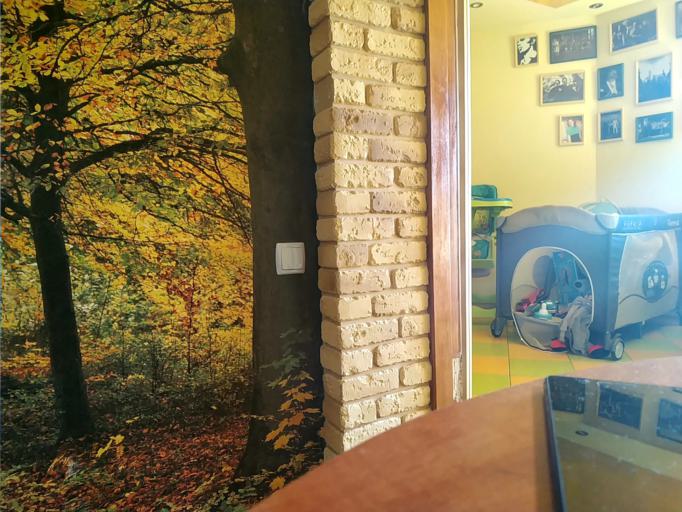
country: RU
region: Tverskaya
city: Torzhok
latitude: 57.0333
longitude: 35.0291
